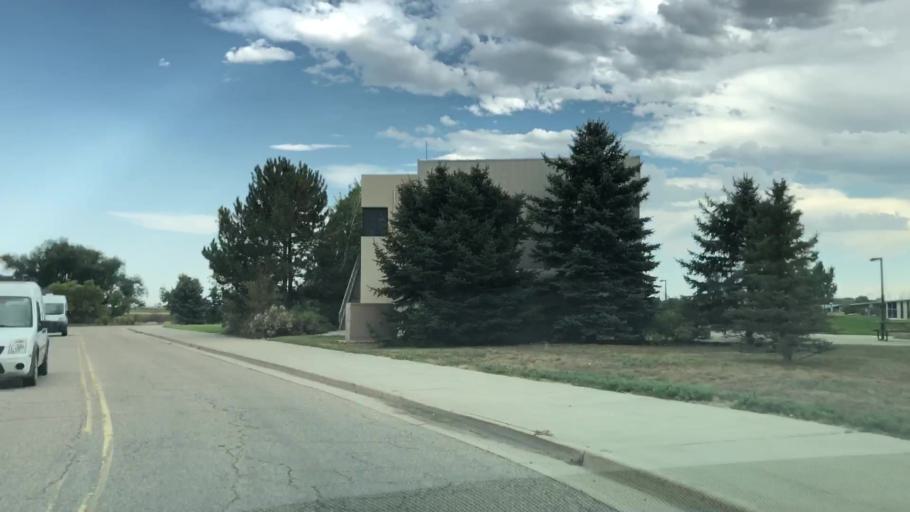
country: US
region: Colorado
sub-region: Larimer County
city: Fort Collins
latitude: 40.5662
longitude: -105.0079
